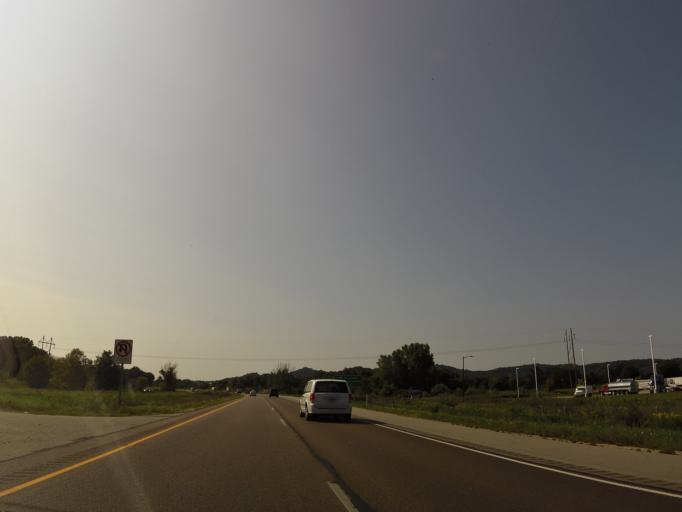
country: US
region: Wisconsin
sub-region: La Crosse County
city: Onalaska
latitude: 43.8748
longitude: -91.1638
